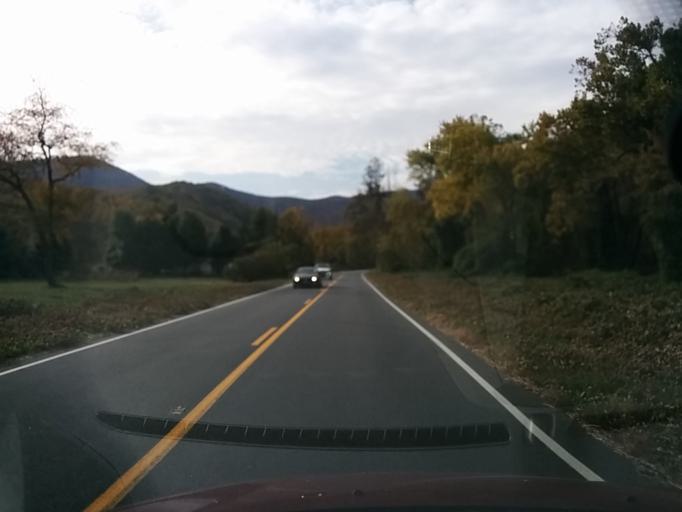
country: US
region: Virginia
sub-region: Nelson County
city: Nellysford
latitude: 37.8780
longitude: -78.9491
